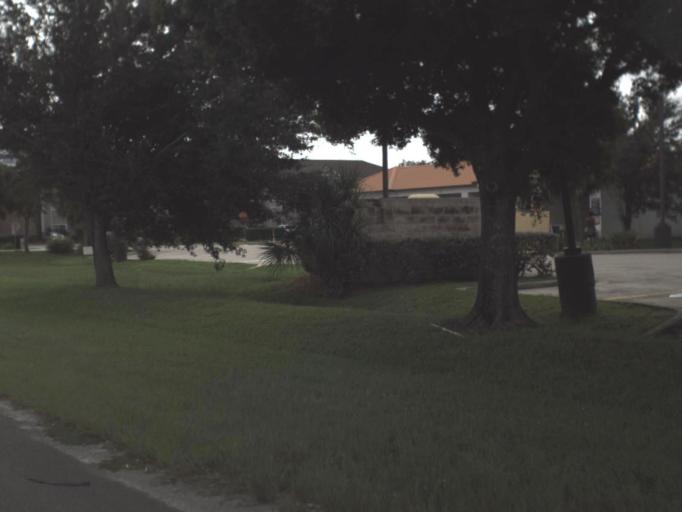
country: US
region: Florida
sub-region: Lee County
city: Fort Myers
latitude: 26.5966
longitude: -81.8505
